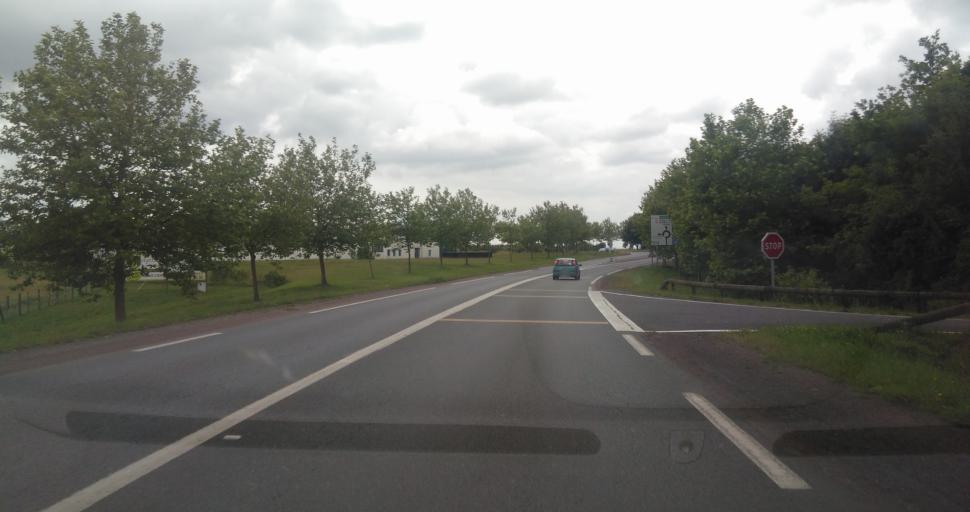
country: FR
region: Pays de la Loire
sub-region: Departement de la Vendee
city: Sainte-Hermine
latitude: 46.5327
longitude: -1.0746
